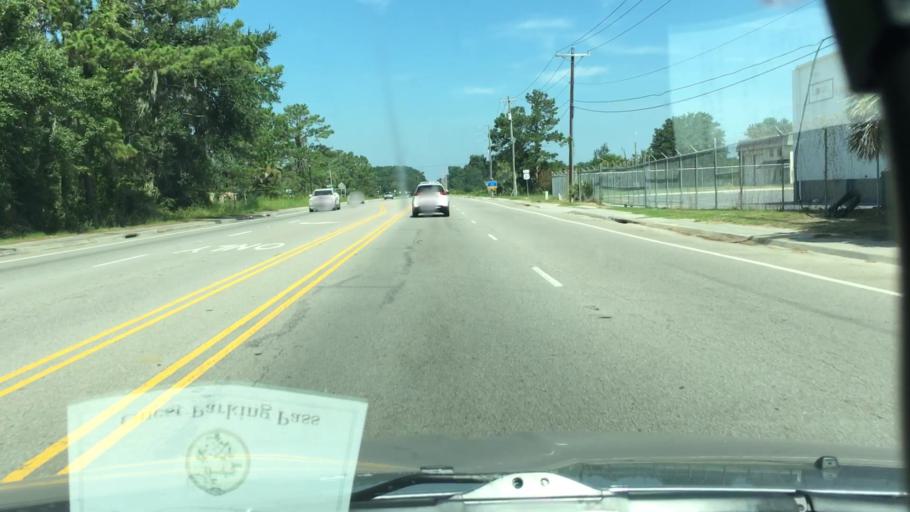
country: US
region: South Carolina
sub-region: Beaufort County
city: Beaufort
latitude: 32.4072
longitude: -80.6370
